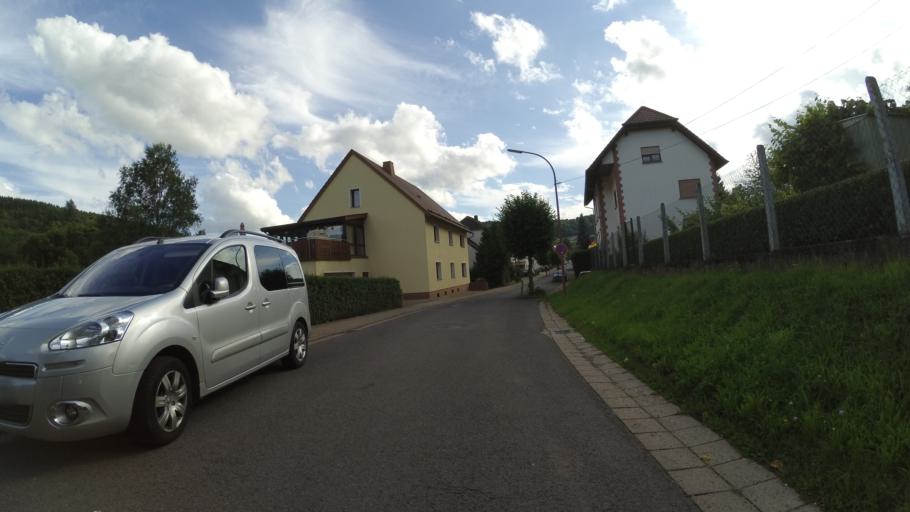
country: DE
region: Saarland
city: Nonnweiler
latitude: 49.5730
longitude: 6.9721
